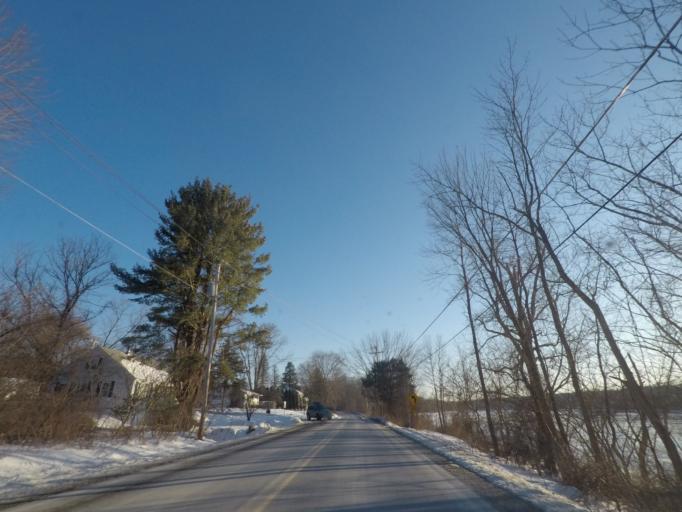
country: US
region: New York
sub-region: Saratoga County
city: Mechanicville
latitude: 42.8695
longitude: -73.6719
